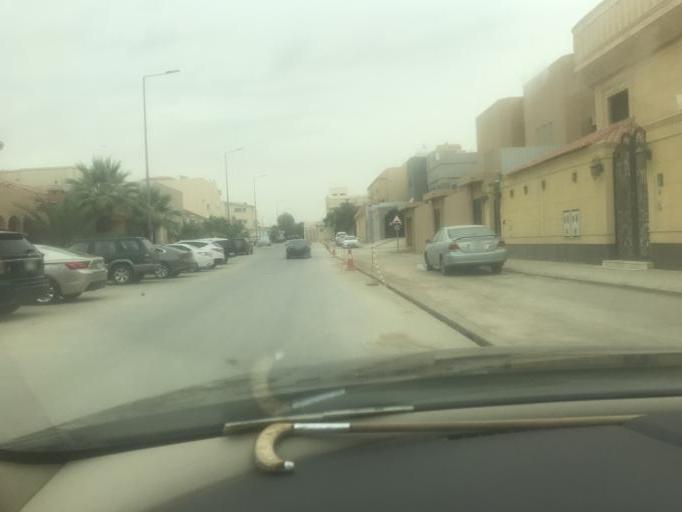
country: SA
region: Ar Riyad
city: Riyadh
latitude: 24.7446
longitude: 46.7656
